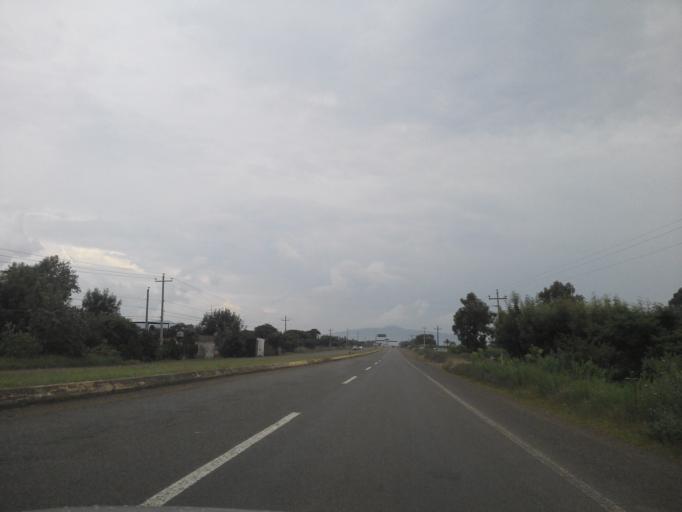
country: MX
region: Jalisco
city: San Jose de Gracia
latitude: 20.7291
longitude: -102.4797
